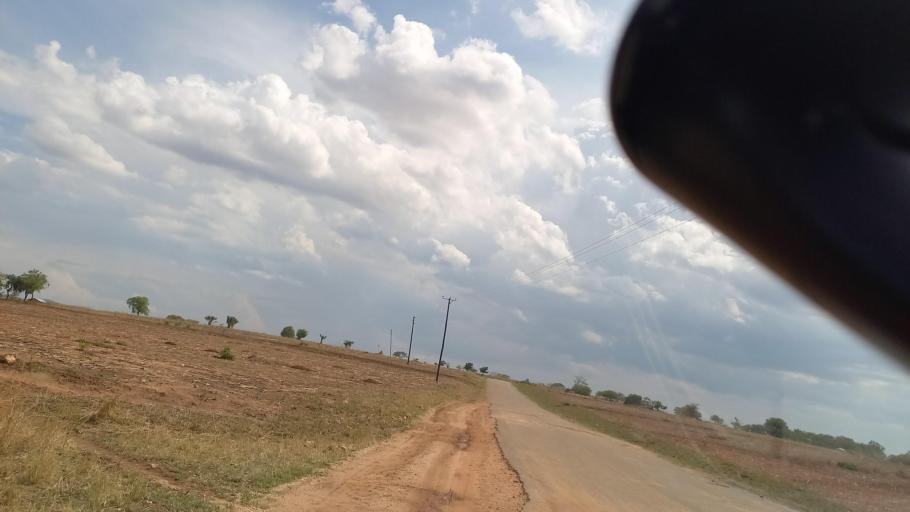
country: ZM
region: Lusaka
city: Kafue
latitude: -16.1818
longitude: 28.0878
